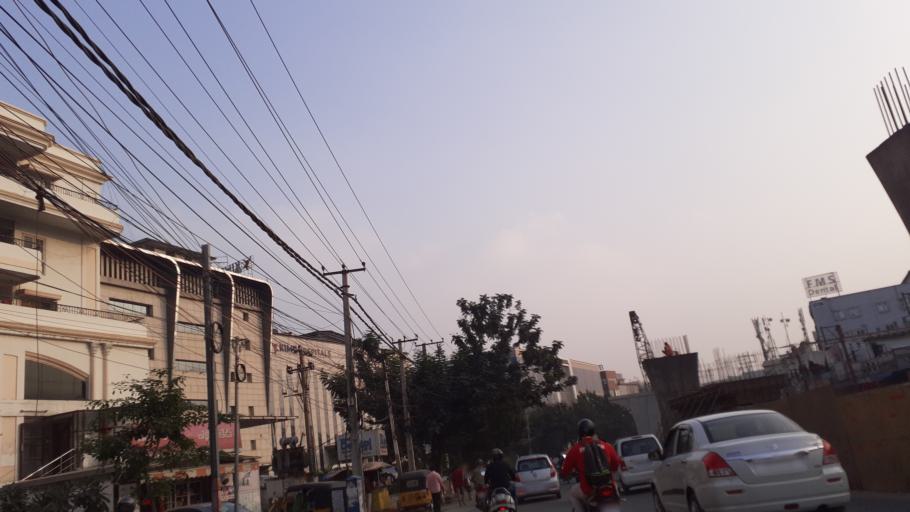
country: IN
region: Telangana
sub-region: Rangareddi
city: Kukatpalli
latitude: 17.4668
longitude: 78.3673
